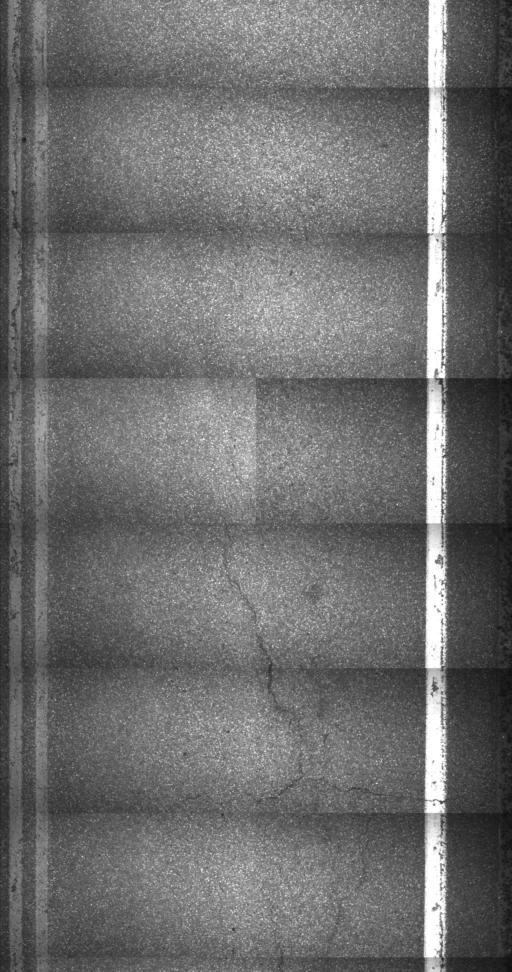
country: US
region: Vermont
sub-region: Addison County
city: Middlebury (village)
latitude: 44.0136
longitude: -73.1002
